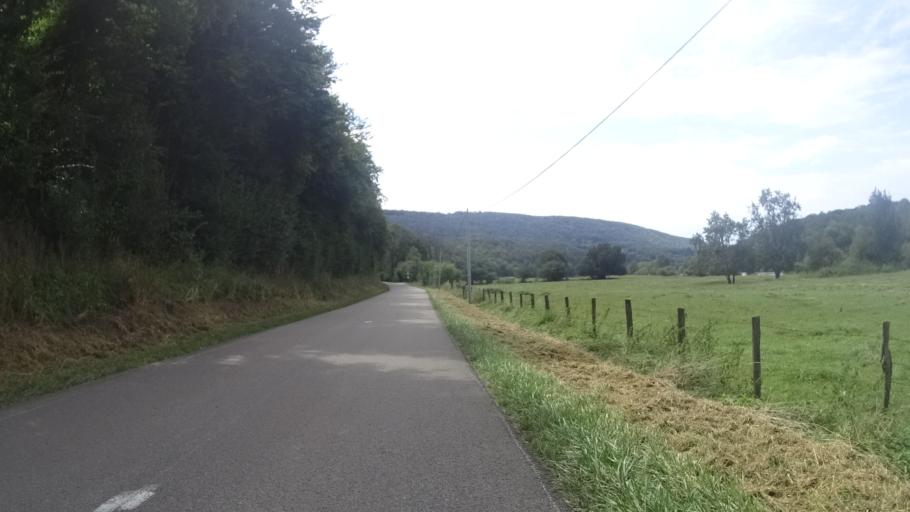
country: FR
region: Franche-Comte
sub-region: Departement du Doubs
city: Clerval
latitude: 47.3754
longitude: 6.5026
